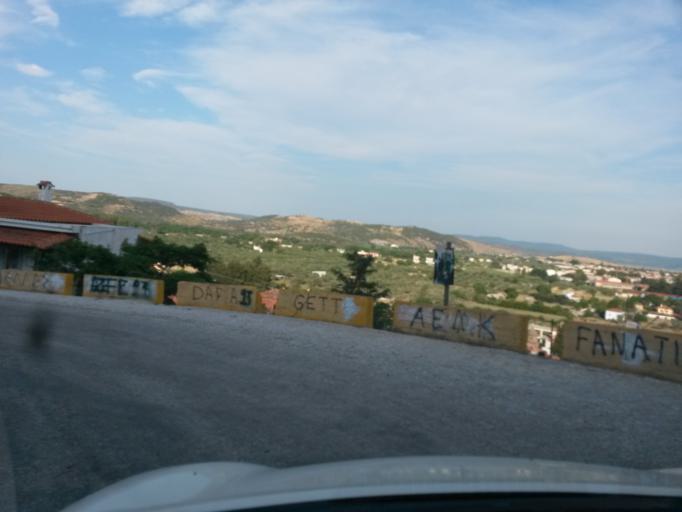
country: GR
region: North Aegean
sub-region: Nomos Lesvou
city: Kalloni
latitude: 39.2402
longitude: 26.1976
